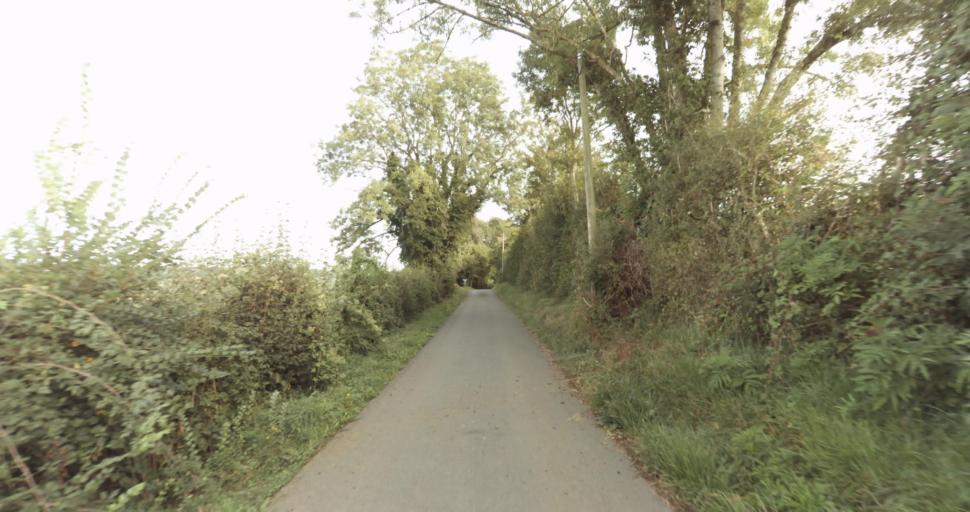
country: FR
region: Lower Normandy
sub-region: Departement de l'Orne
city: Vimoutiers
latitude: 48.8781
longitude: 0.2260
